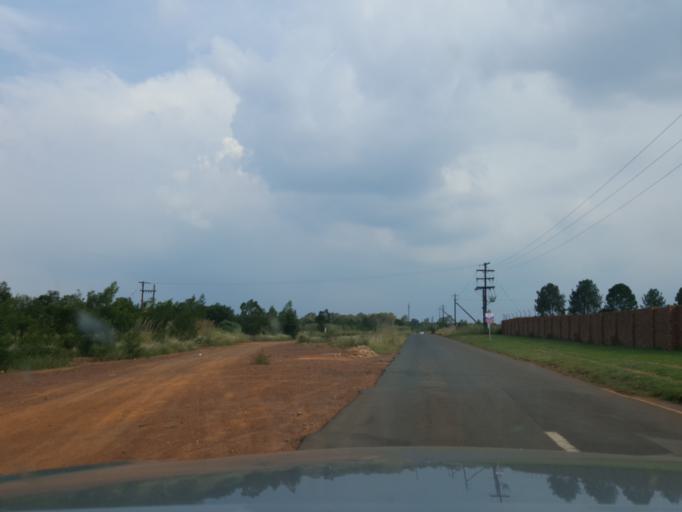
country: ZA
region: Gauteng
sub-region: City of Tshwane Metropolitan Municipality
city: Centurion
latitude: -25.8588
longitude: 28.3267
